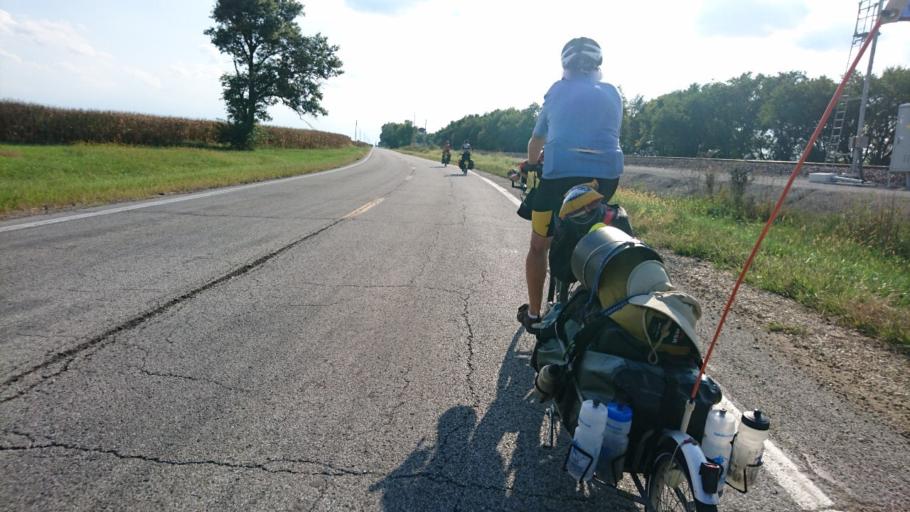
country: US
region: Illinois
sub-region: Logan County
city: Atlanta
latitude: 40.3112
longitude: -89.1733
